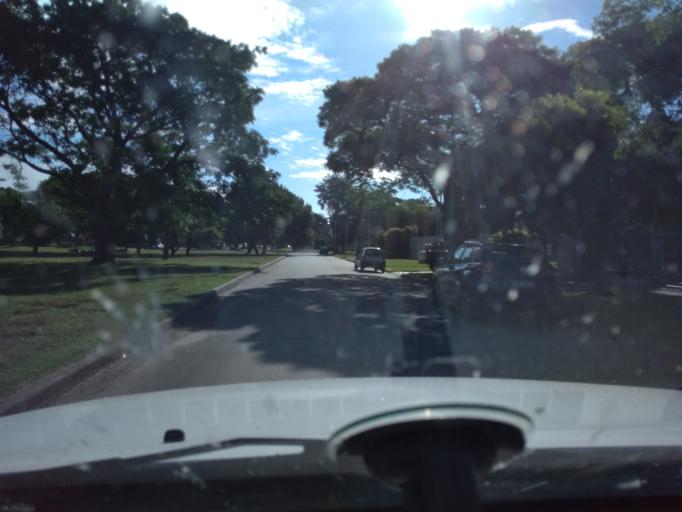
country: UY
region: Canelones
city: Paso de Carrasco
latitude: -34.8882
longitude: -56.0689
